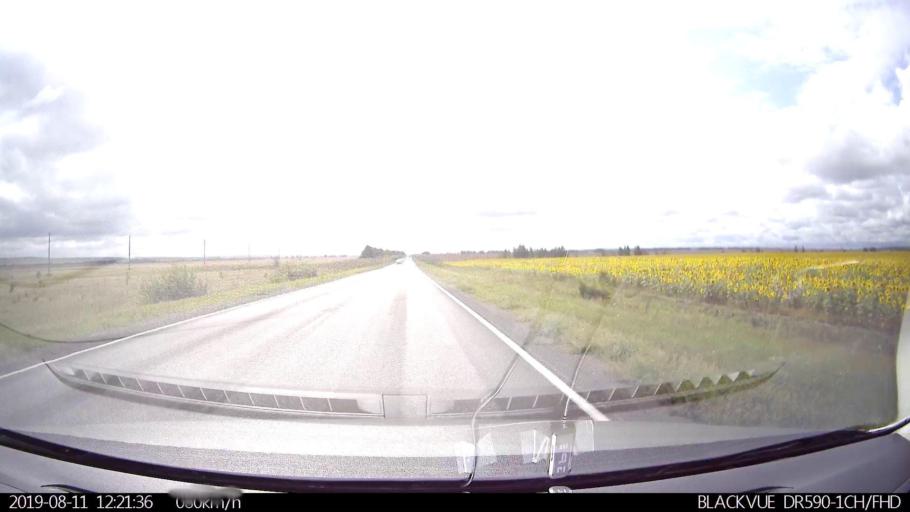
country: RU
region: Ulyanovsk
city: Ignatovka
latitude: 53.9191
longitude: 47.9573
